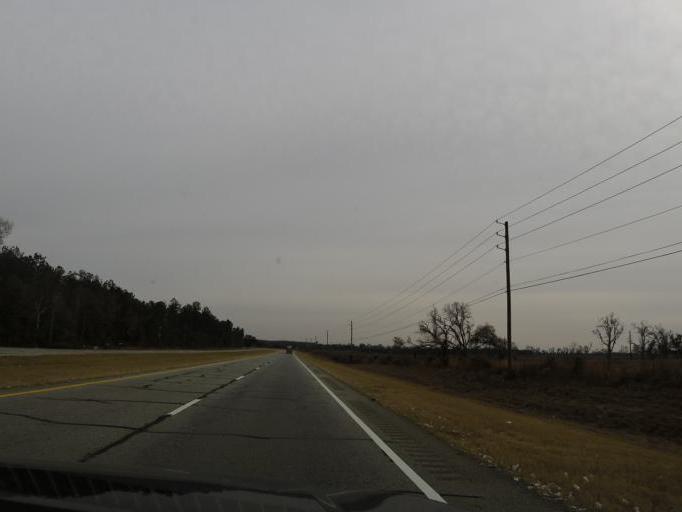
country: US
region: Georgia
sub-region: Decatur County
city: Bainbridge
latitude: 30.9491
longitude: -84.7024
